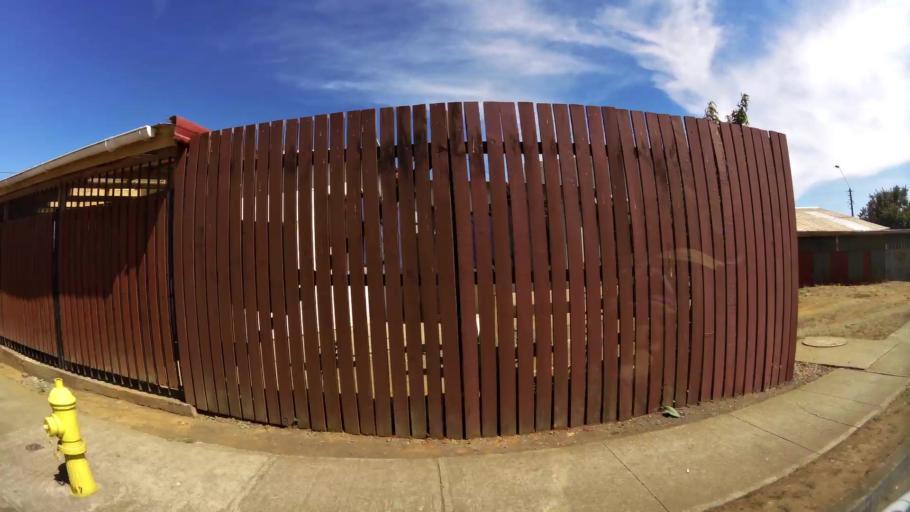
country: CL
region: Biobio
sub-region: Provincia de Concepcion
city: Talcahuano
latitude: -36.7110
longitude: -73.1302
